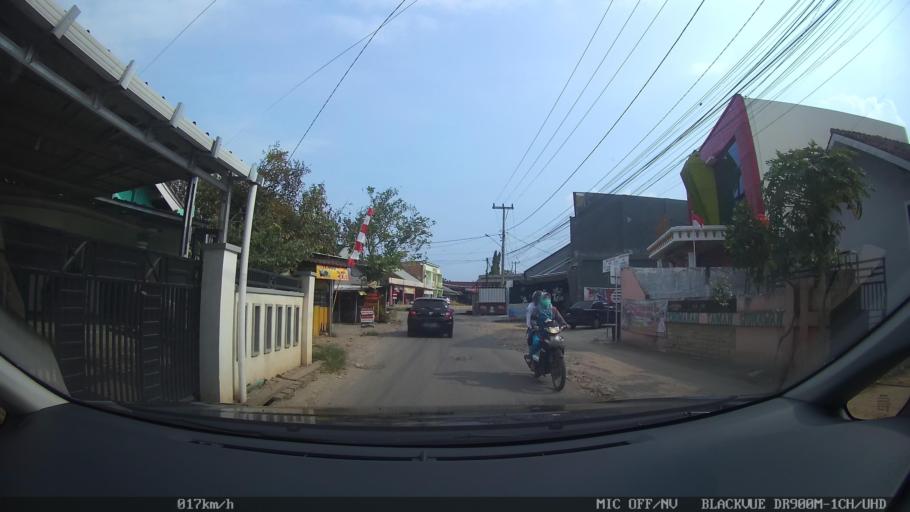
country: ID
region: Lampung
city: Kedaton
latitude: -5.3681
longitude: 105.2211
